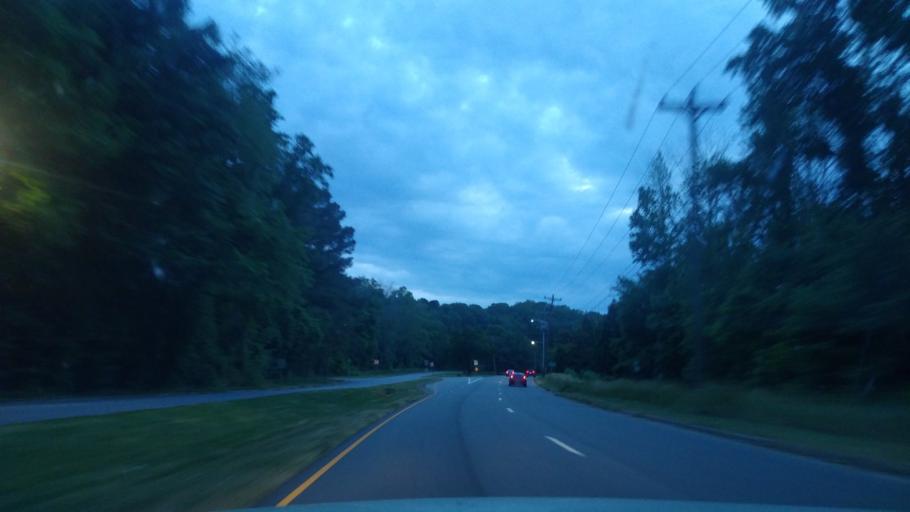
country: US
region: North Carolina
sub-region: Guilford County
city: Greensboro
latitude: 36.1062
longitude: -79.8000
